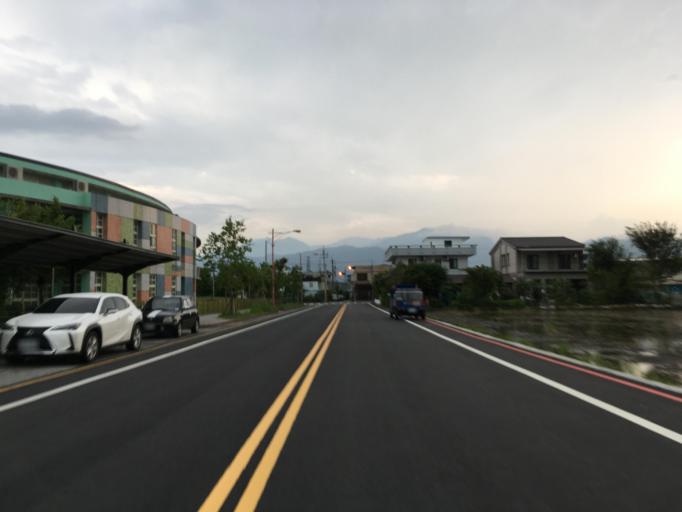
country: TW
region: Taiwan
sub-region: Yilan
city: Yilan
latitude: 24.6637
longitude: 121.7632
